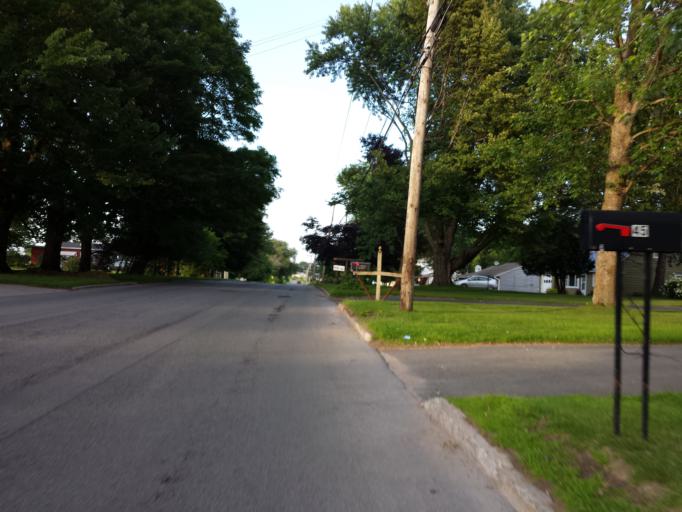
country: US
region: New York
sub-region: St. Lawrence County
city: Potsdam
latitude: 44.6865
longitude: -74.9811
